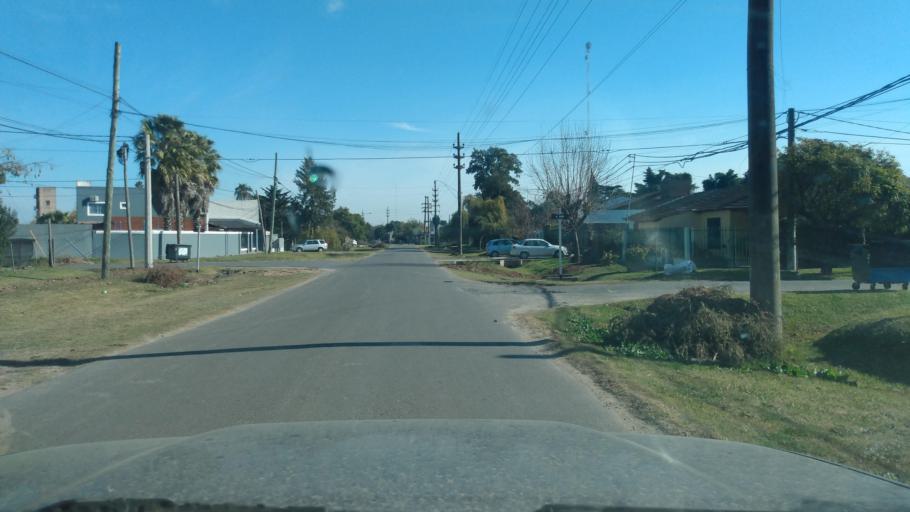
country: AR
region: Buenos Aires
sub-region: Partido de Lujan
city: Lujan
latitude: -34.5780
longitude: -59.0998
